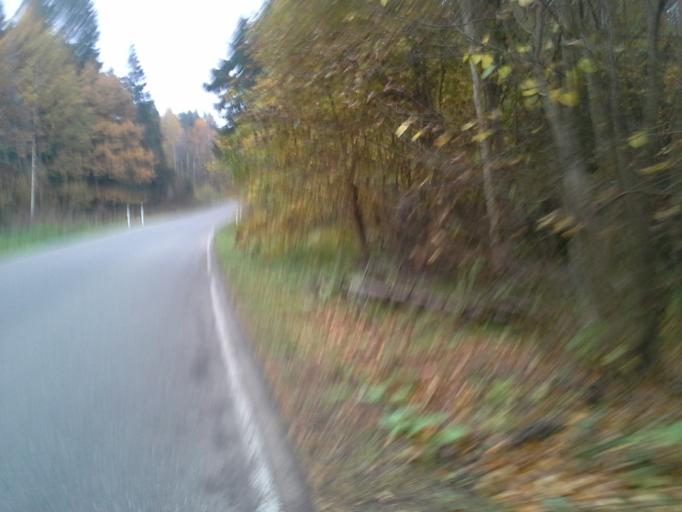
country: RU
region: Moskovskaya
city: Nazar'yevo
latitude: 55.6933
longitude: 36.9766
